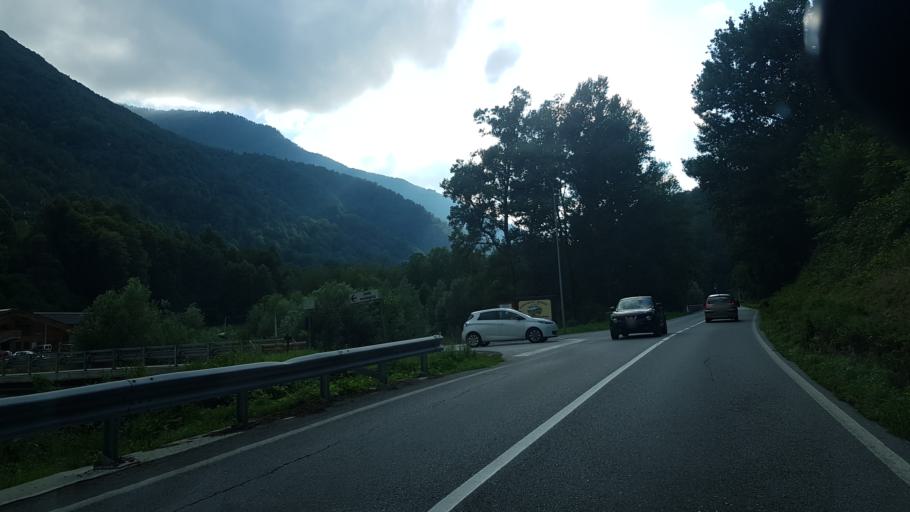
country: IT
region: Piedmont
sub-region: Provincia di Cuneo
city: Frassino
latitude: 44.5712
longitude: 7.2639
